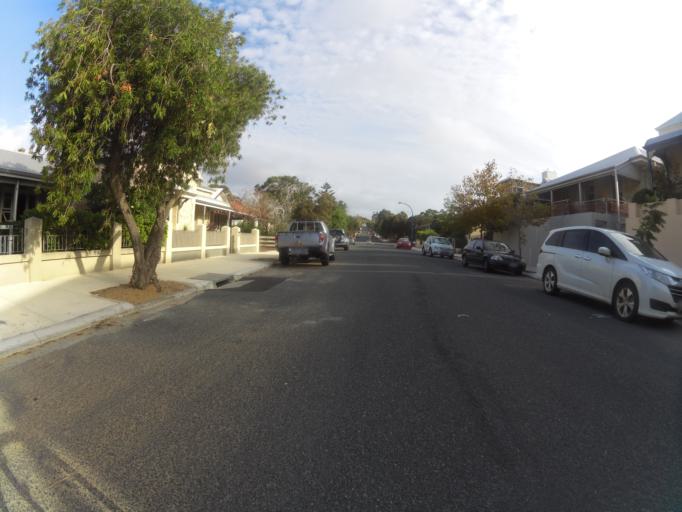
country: AU
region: Western Australia
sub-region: East Fremantle
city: East Fremantle
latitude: -32.0433
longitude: 115.7591
